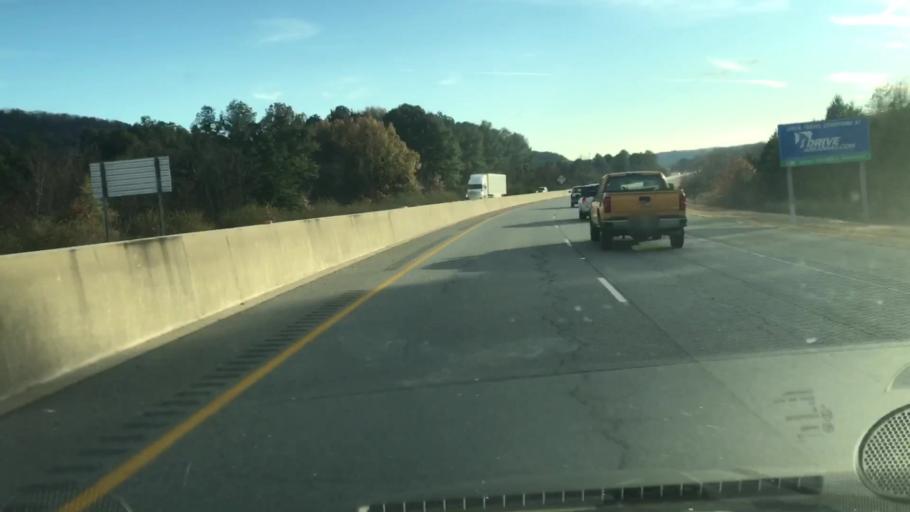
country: US
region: Arkansas
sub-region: Garland County
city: Hot Springs
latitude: 34.4943
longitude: -92.9762
